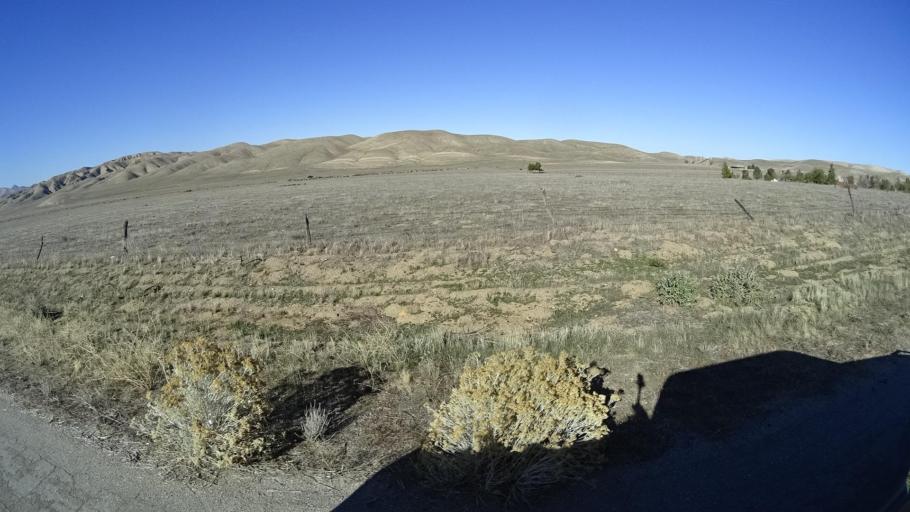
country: US
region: California
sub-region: Kern County
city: Maricopa
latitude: 34.9365
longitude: -119.4597
